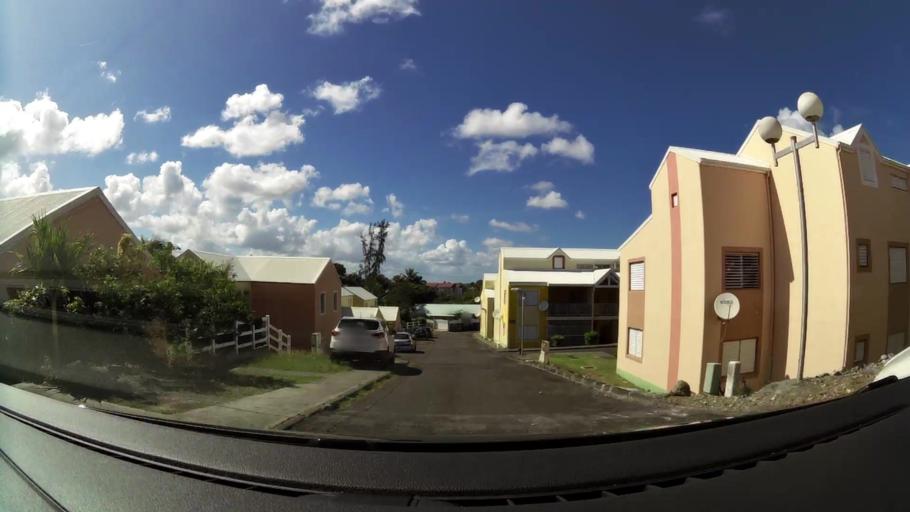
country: GP
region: Guadeloupe
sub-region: Guadeloupe
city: Le Moule
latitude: 16.3272
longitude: -61.3517
